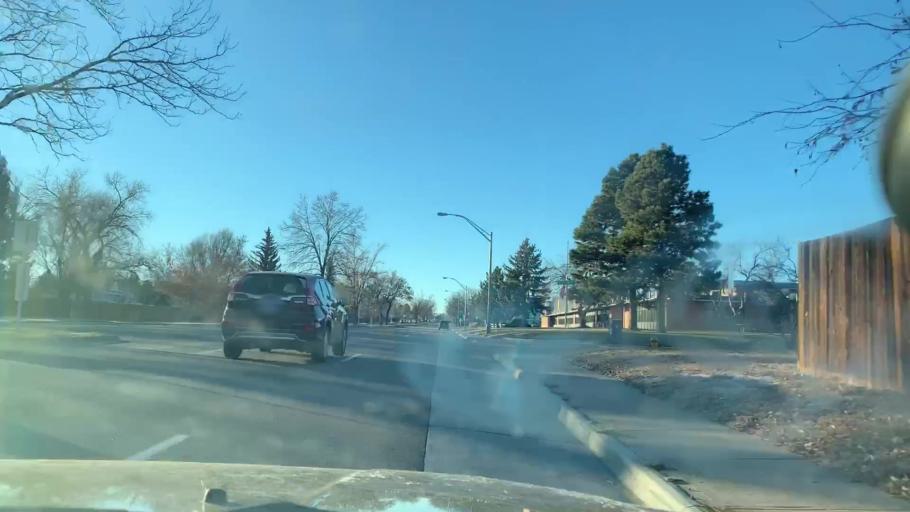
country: US
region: Colorado
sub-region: Arapahoe County
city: Cherry Hills Village
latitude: 39.6582
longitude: -104.9130
